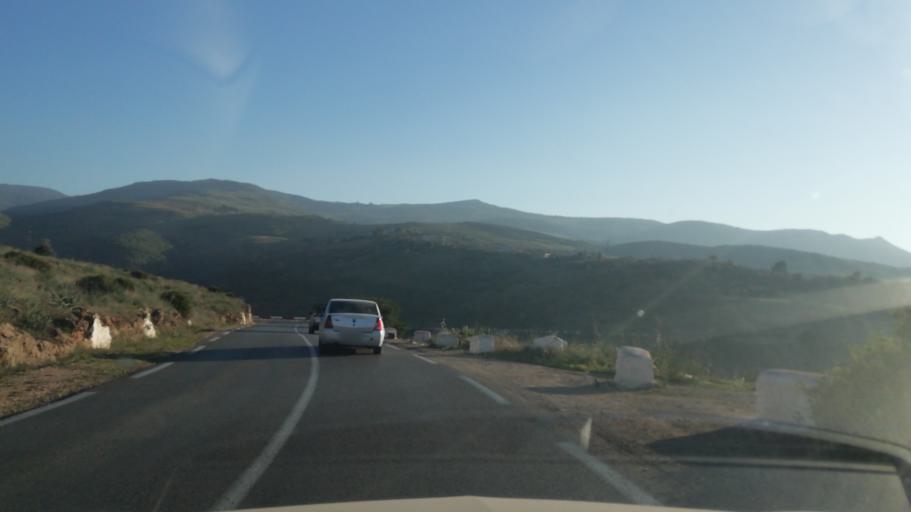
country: DZ
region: Tlemcen
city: Beni Mester
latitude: 34.8448
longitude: -1.4666
